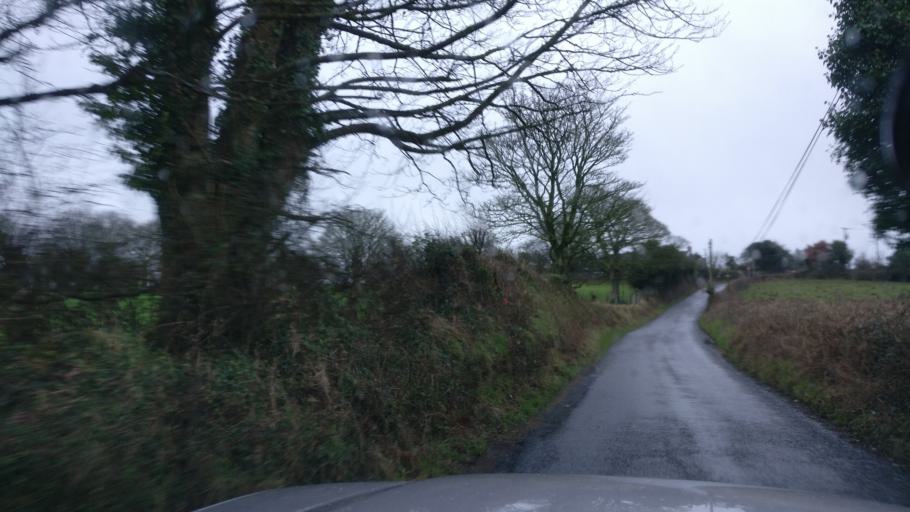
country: IE
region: Connaught
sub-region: County Galway
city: Loughrea
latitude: 53.1727
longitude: -8.6464
